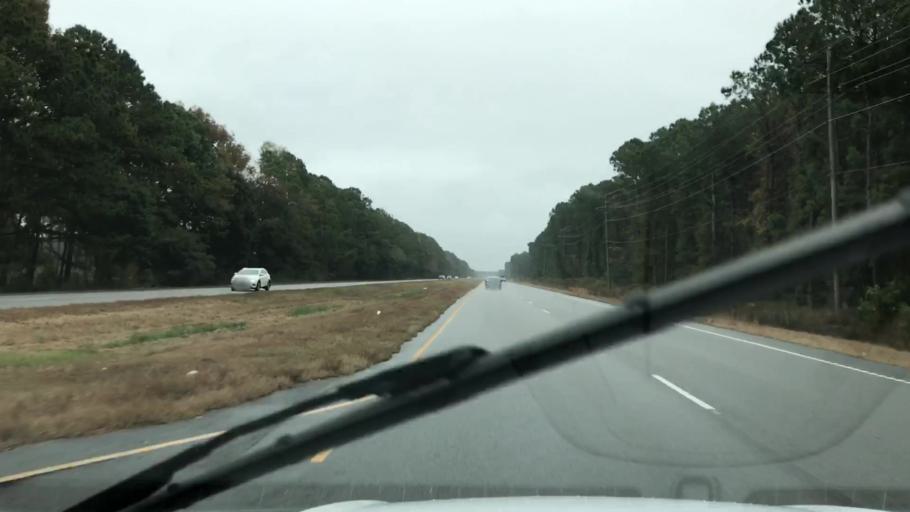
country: US
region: South Carolina
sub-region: Charleston County
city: Isle of Palms
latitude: 32.9027
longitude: -79.7291
